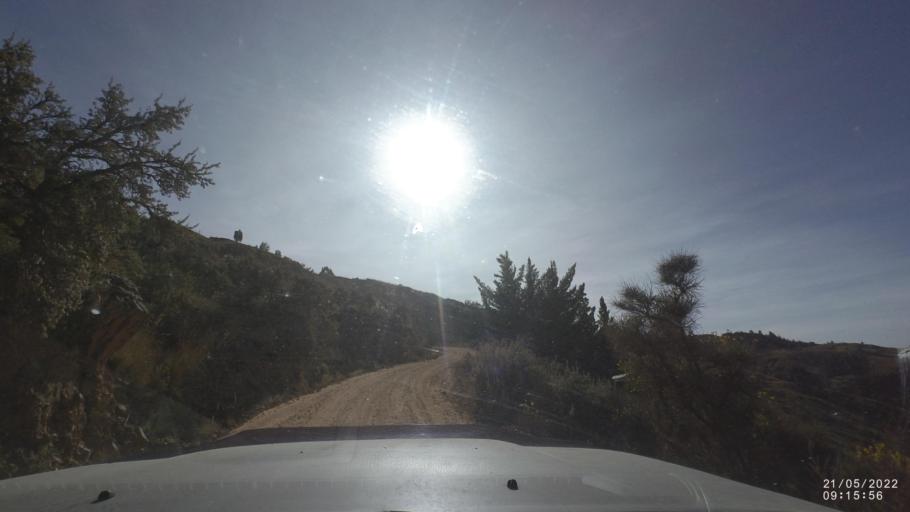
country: BO
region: Cochabamba
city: Cochabamba
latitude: -17.3640
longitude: -66.0254
